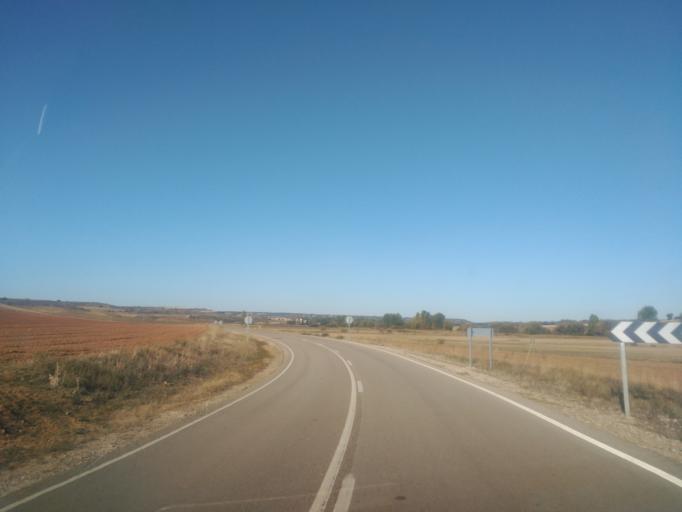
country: ES
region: Castille and Leon
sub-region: Provincia de Soria
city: Espeja de San Marcelino
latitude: 41.7574
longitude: -3.2443
